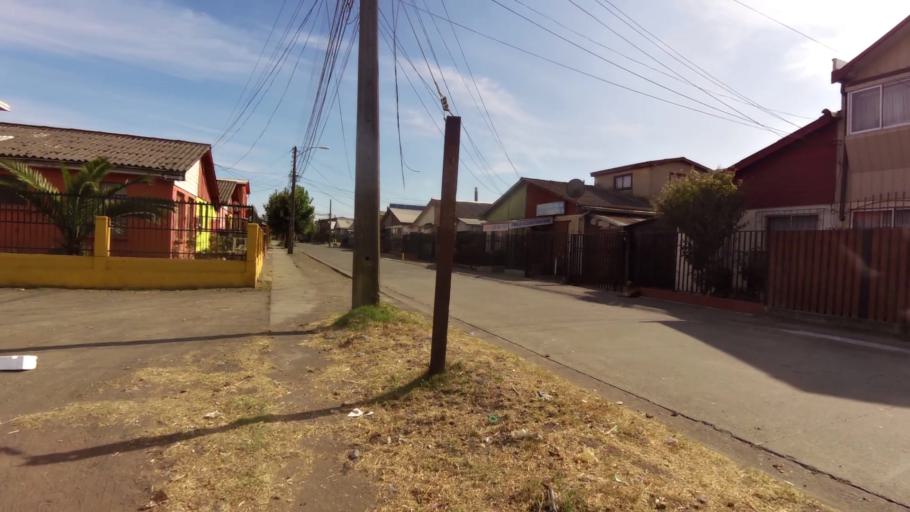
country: CL
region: Biobio
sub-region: Provincia de Concepcion
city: Talcahuano
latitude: -36.7845
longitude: -73.1075
